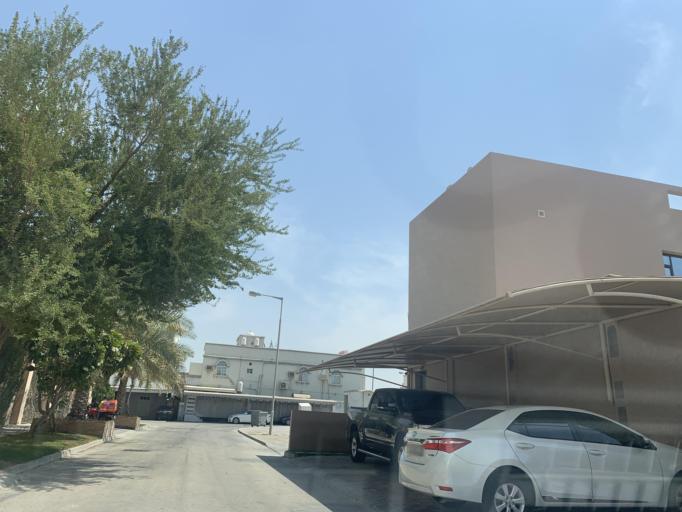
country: BH
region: Central Governorate
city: Madinat Hamad
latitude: 26.1393
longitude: 50.5055
